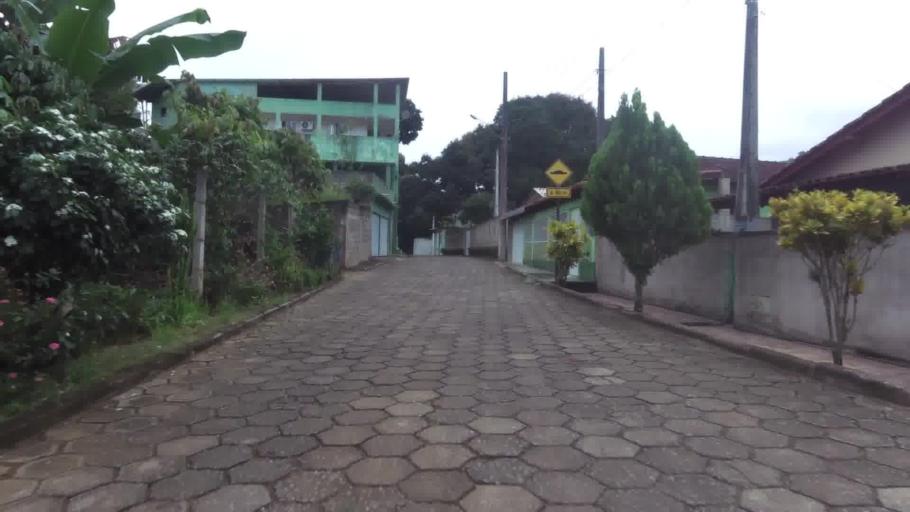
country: BR
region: Espirito Santo
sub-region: Iconha
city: Iconha
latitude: -20.7753
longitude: -40.8281
